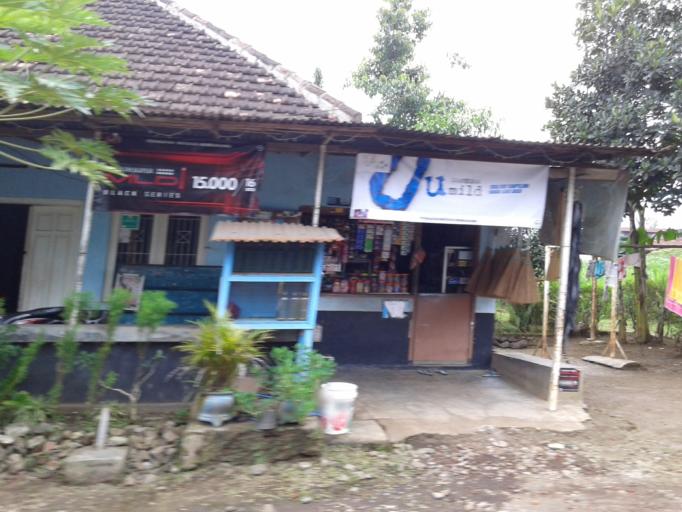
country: ID
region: East Java
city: Singosari
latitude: -7.8899
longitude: 112.6696
